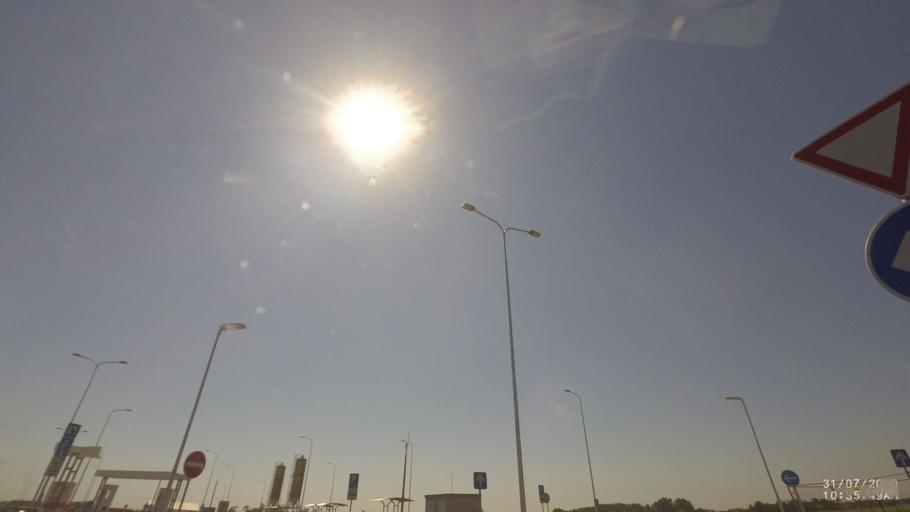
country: SK
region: Trnavsky
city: Samorin
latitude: 48.0114
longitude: 17.4556
